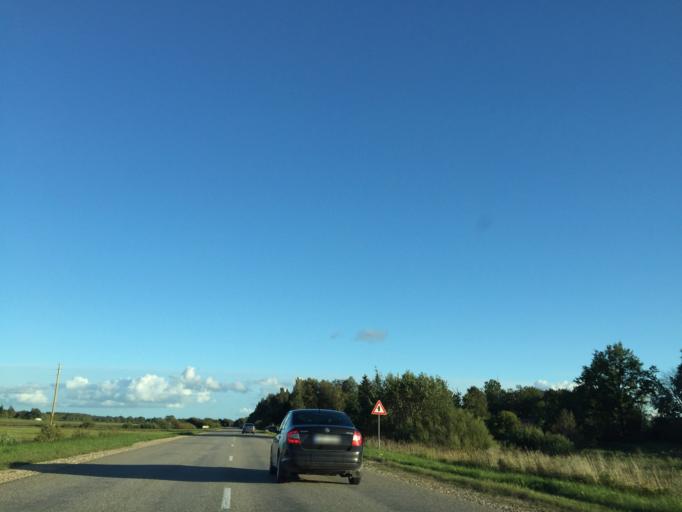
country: LV
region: Kuldigas Rajons
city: Kuldiga
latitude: 56.9549
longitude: 22.0081
